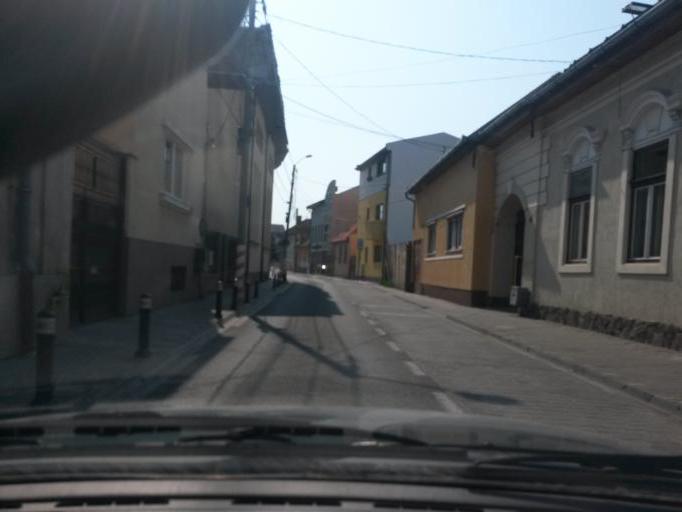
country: RO
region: Mures
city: Targu-Mures
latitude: 46.5486
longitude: 24.5574
